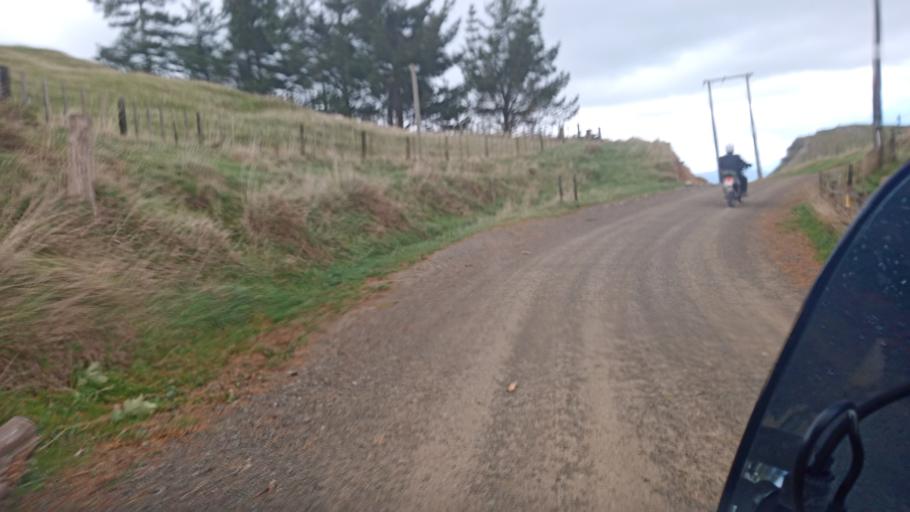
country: NZ
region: Gisborne
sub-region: Gisborne District
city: Gisborne
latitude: -38.4837
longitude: 177.6069
